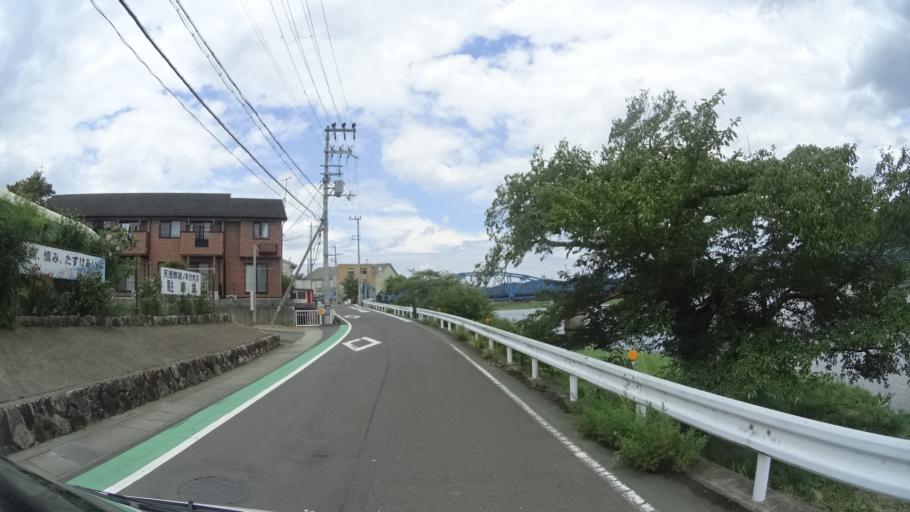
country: JP
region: Kyoto
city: Ayabe
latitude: 35.2953
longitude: 135.2636
